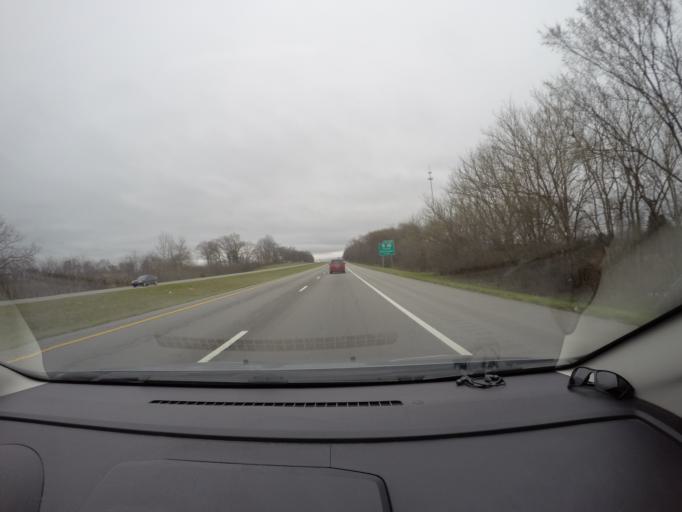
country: US
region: Tennessee
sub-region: Marion County
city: Monteagle
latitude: 35.3138
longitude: -85.9160
